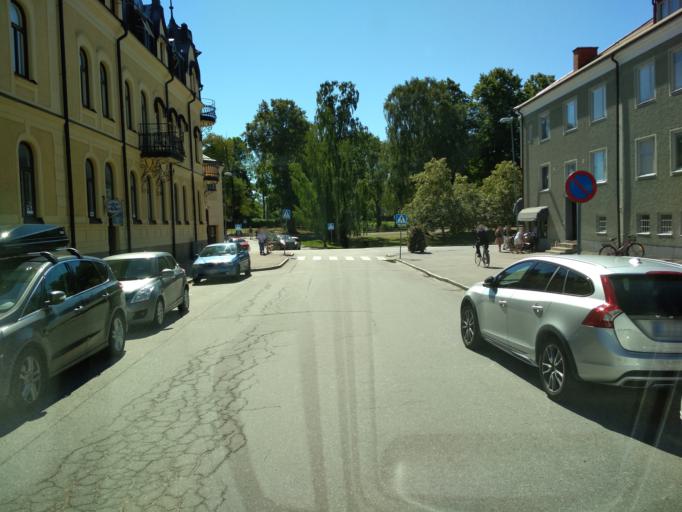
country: SE
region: Soedermanland
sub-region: Strangnas Kommun
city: Mariefred
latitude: 59.2597
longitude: 17.2196
